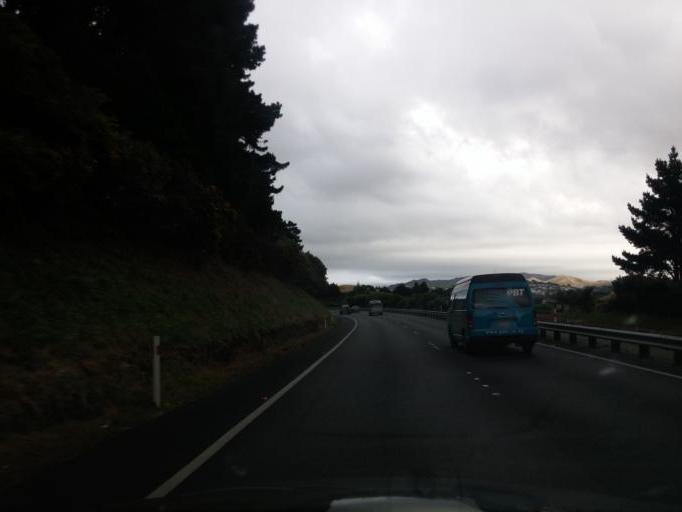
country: NZ
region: Wellington
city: Petone
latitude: -41.1970
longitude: 174.8254
